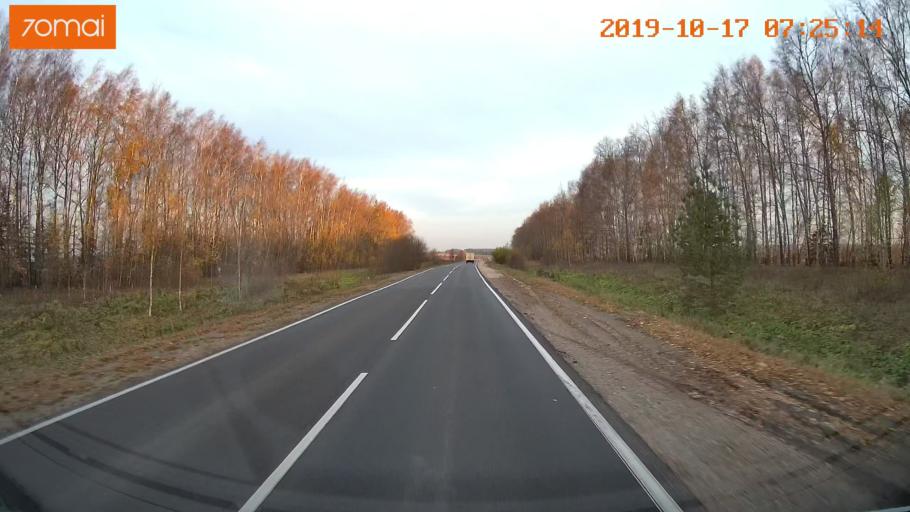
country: RU
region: Ivanovo
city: Gavrilov Posad
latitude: 56.3478
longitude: 40.1077
